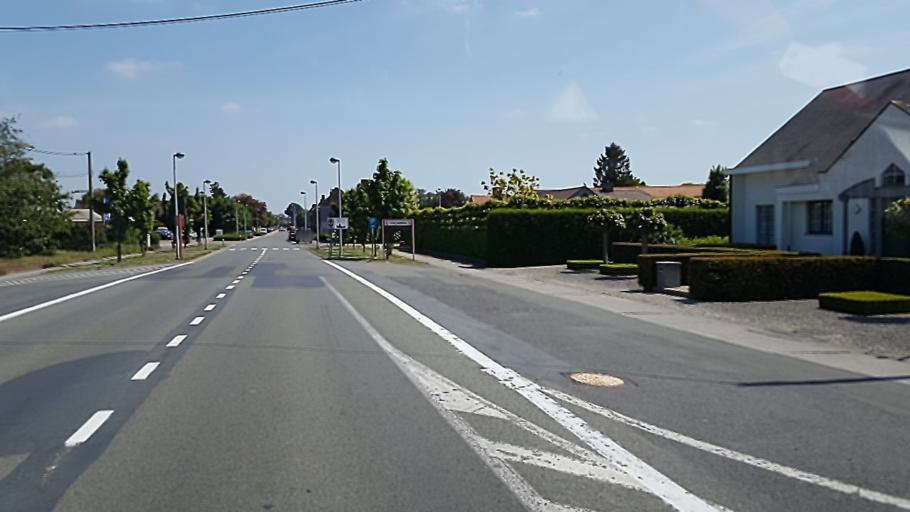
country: BE
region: Flanders
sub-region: Provincie West-Vlaanderen
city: Wervik
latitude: 50.8125
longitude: 3.0665
